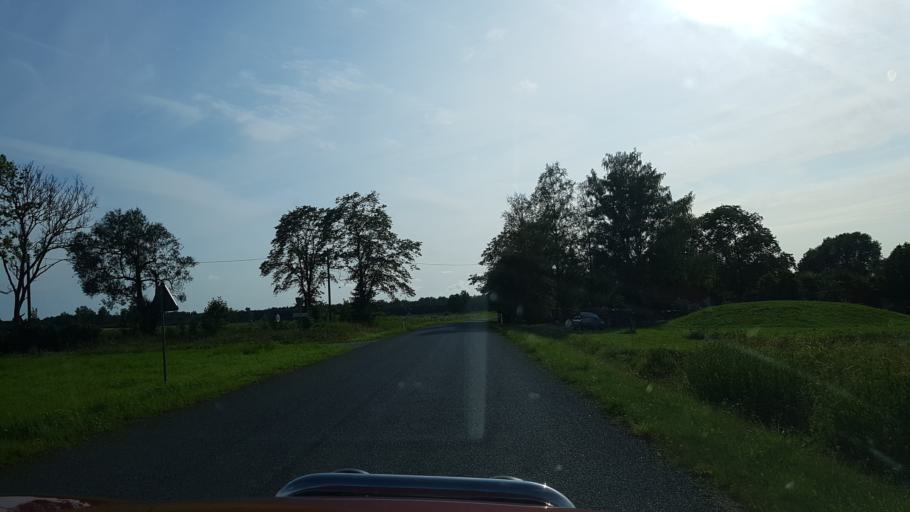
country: EE
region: Laeaene
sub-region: Lihula vald
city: Lihula
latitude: 58.3814
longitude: 24.0046
